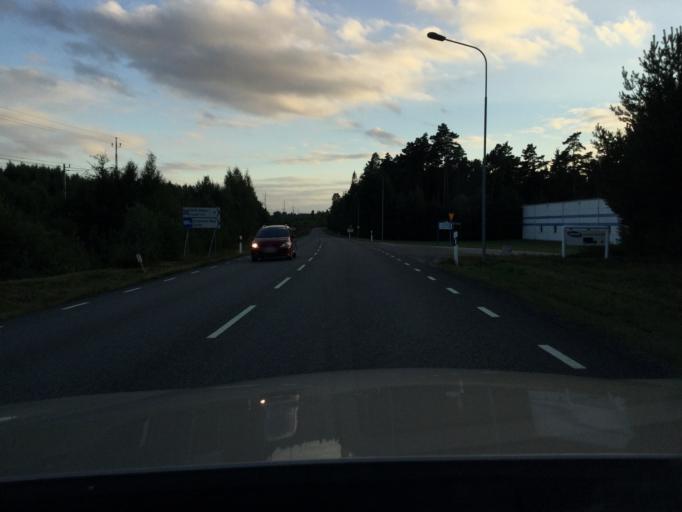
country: SE
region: Kronoberg
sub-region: Almhults Kommun
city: AElmhult
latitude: 56.6323
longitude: 14.2118
